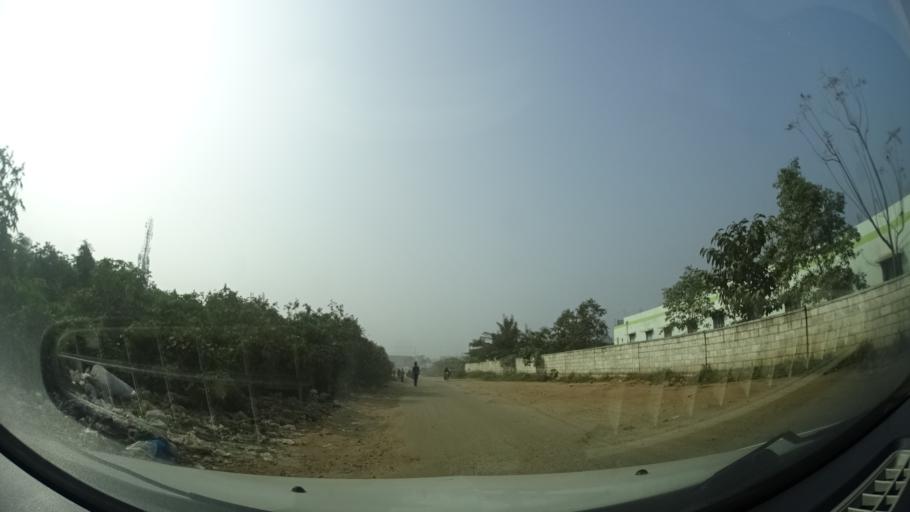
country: IN
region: Karnataka
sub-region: Bangalore Urban
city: Anekal
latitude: 12.8175
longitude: 77.6683
